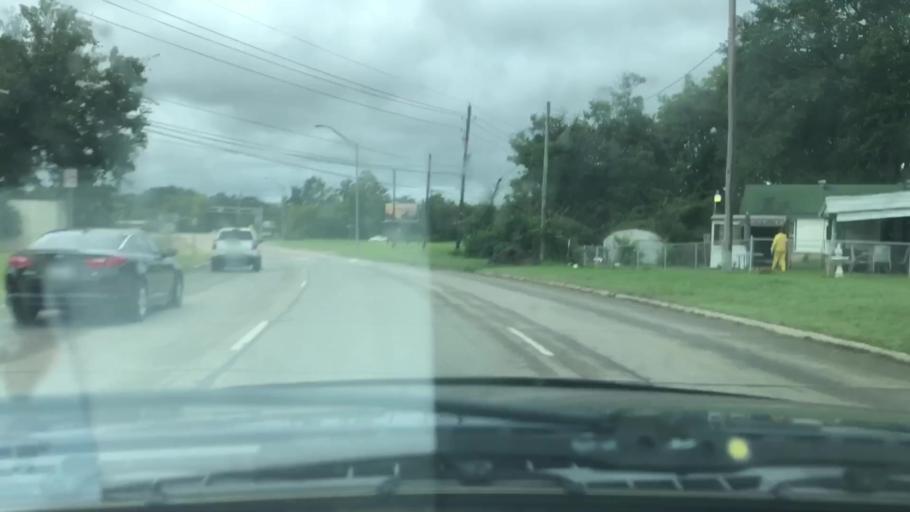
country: US
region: Texas
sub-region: Bowie County
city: Texarkana
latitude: 33.4238
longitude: -94.0694
